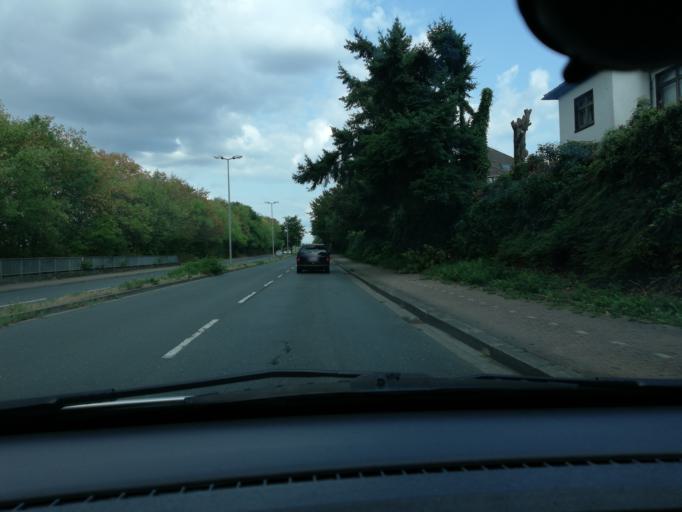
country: DE
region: North Rhine-Westphalia
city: Hattingen
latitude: 51.4033
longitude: 7.1847
